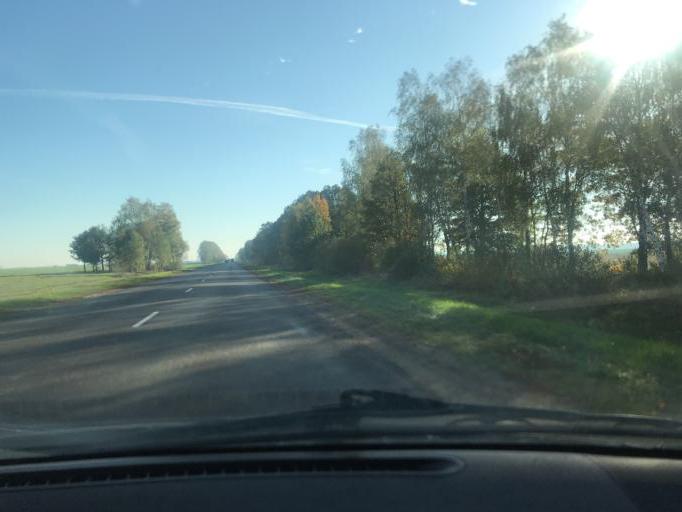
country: BY
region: Brest
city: Ivanava
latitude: 52.1456
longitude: 25.4718
